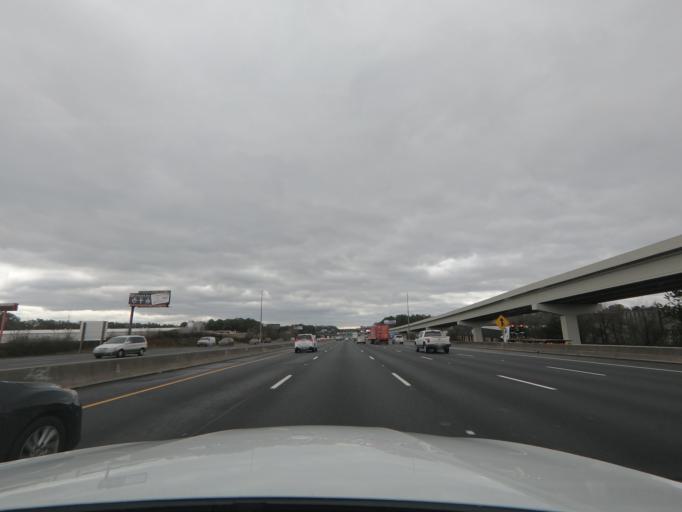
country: US
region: Georgia
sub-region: Cobb County
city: Marietta
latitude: 33.9778
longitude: -84.5347
